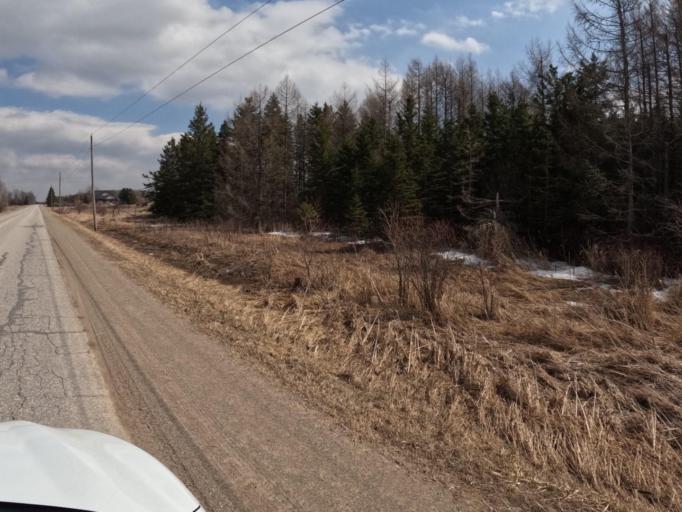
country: CA
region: Ontario
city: Shelburne
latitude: 44.0162
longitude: -80.1765
